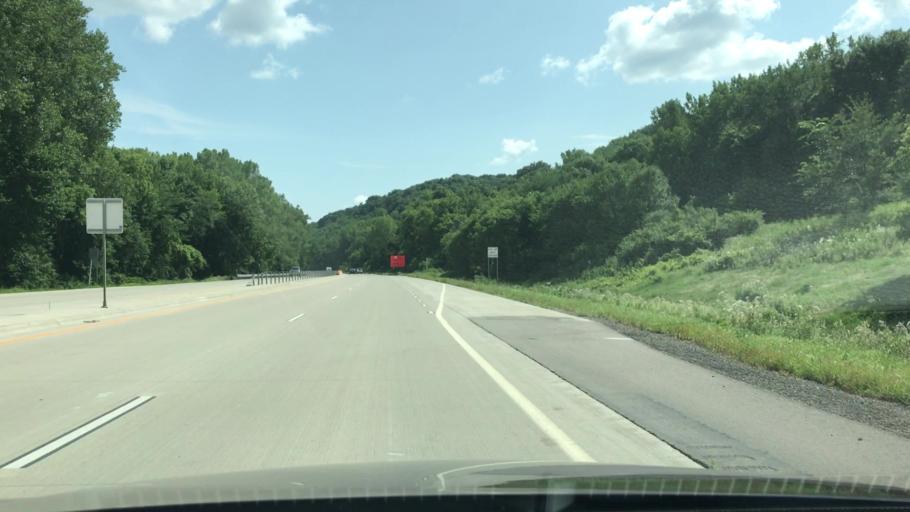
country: US
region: Minnesota
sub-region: Nicollet County
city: North Mankato
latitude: 44.2189
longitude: -94.0276
